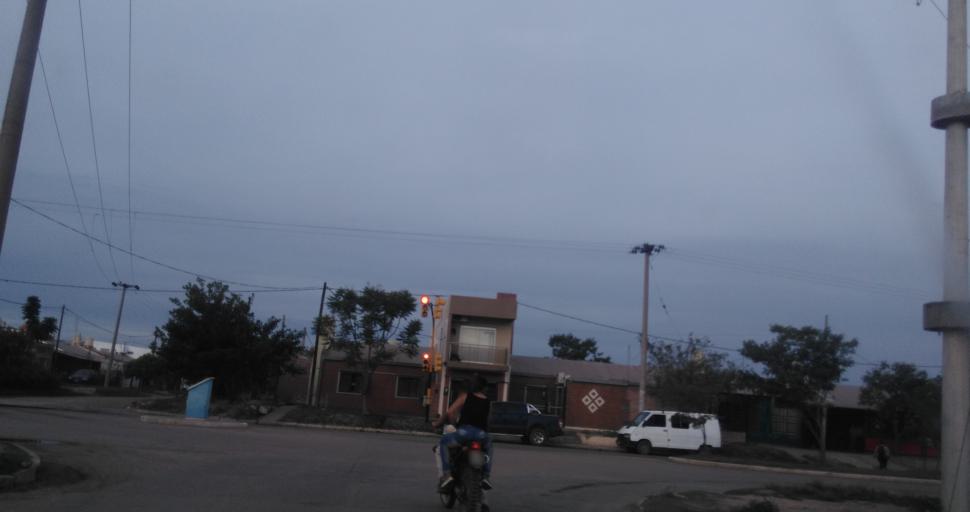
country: AR
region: Chaco
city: Fontana
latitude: -27.4134
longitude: -59.0294
